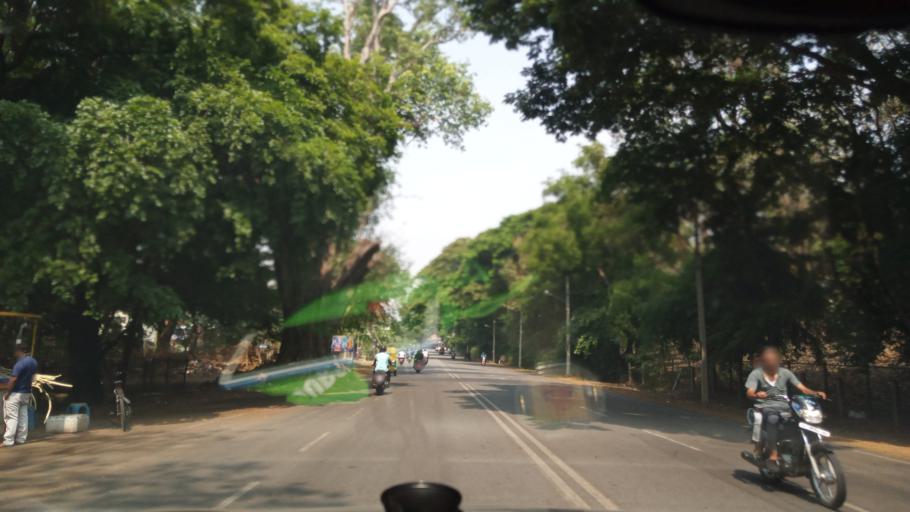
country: IN
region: Karnataka
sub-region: Mysore
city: Mysore
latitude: 12.3070
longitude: 76.6344
